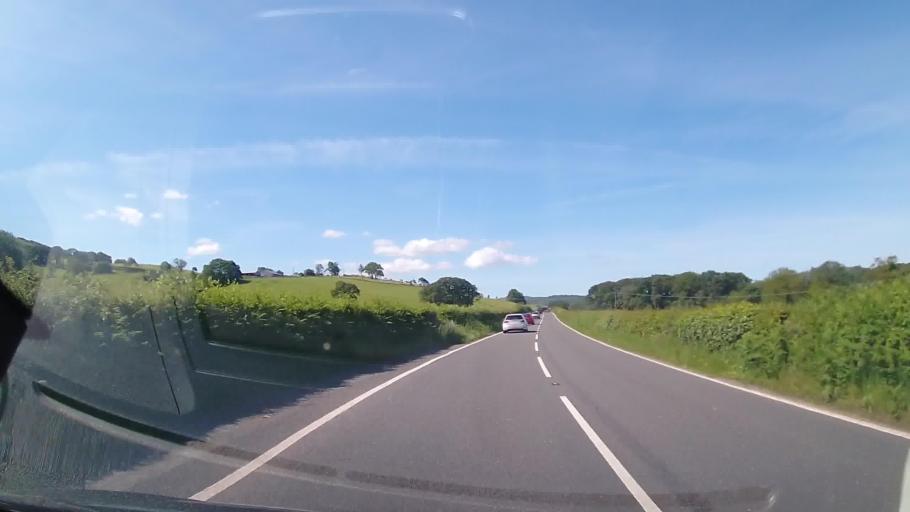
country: GB
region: Wales
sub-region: Sir Powys
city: Machynlleth
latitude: 52.6025
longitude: -3.7935
